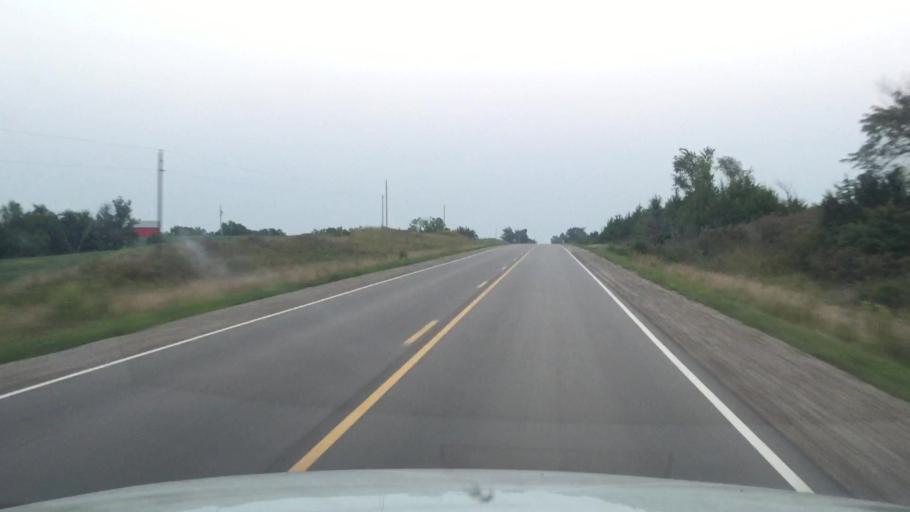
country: US
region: Iowa
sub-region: Marion County
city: Melcher-Dallas
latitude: 41.1895
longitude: -93.4181
